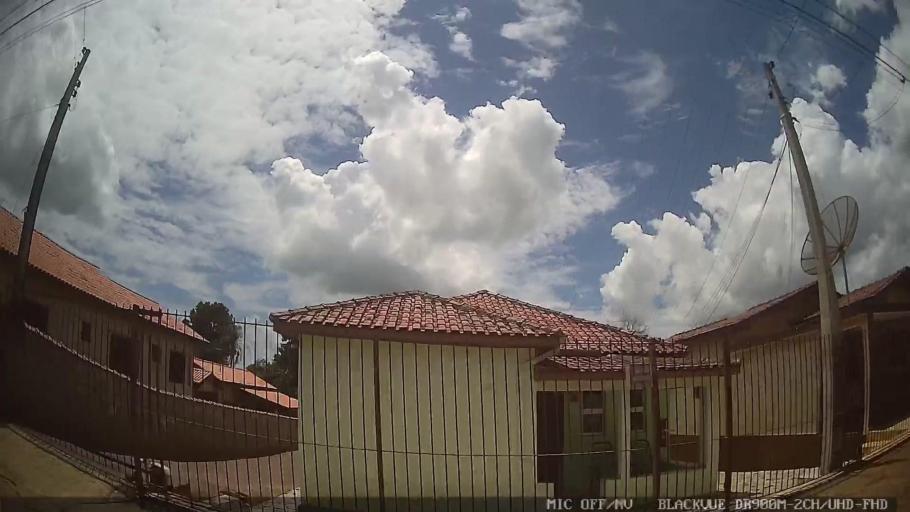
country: BR
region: Sao Paulo
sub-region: Laranjal Paulista
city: Laranjal Paulista
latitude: -23.0377
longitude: -47.8873
